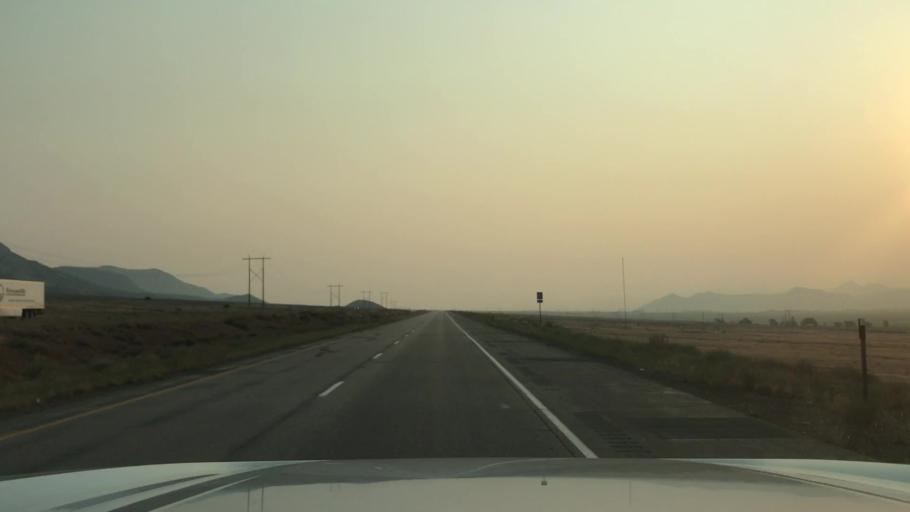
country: US
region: Utah
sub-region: Sevier County
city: Richfield
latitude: 38.8133
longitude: -112.0540
